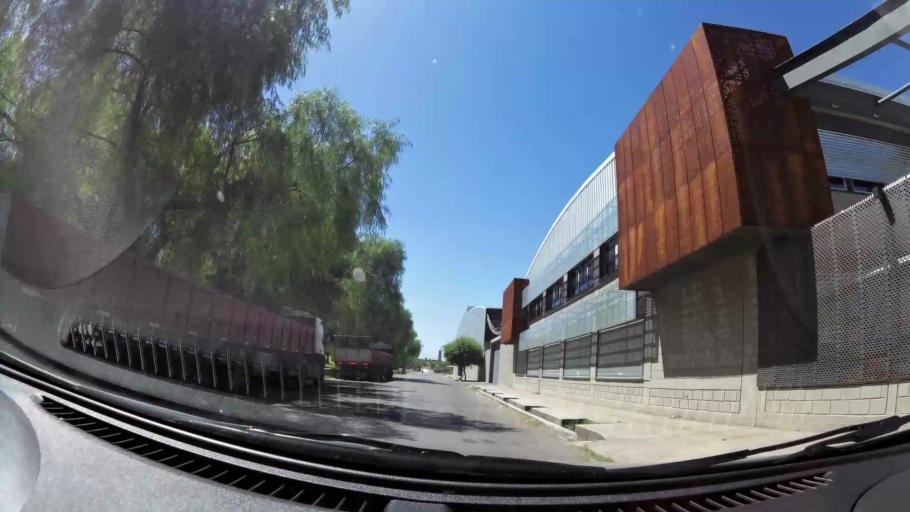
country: AR
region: San Juan
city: San Juan
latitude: -31.5229
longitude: -68.5405
